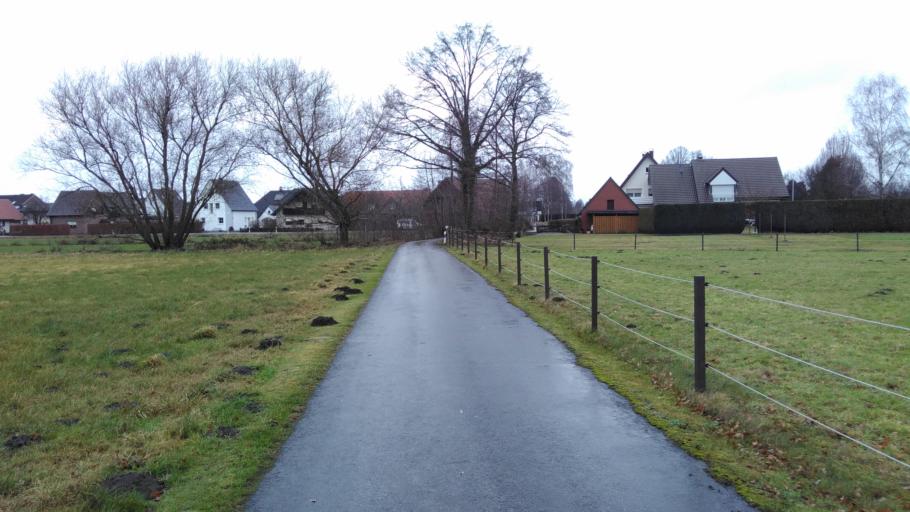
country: DE
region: North Rhine-Westphalia
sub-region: Regierungsbezirk Detmold
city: Verl
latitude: 51.8722
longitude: 8.4886
